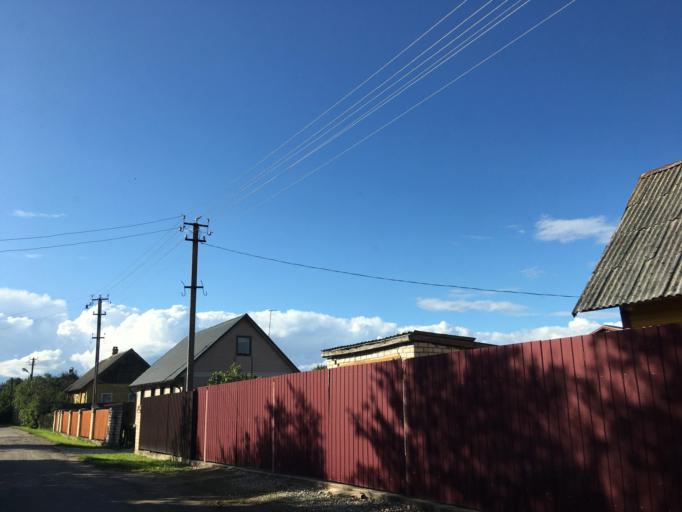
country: RU
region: Pskov
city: Izborsk
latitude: 57.7712
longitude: 27.9766
